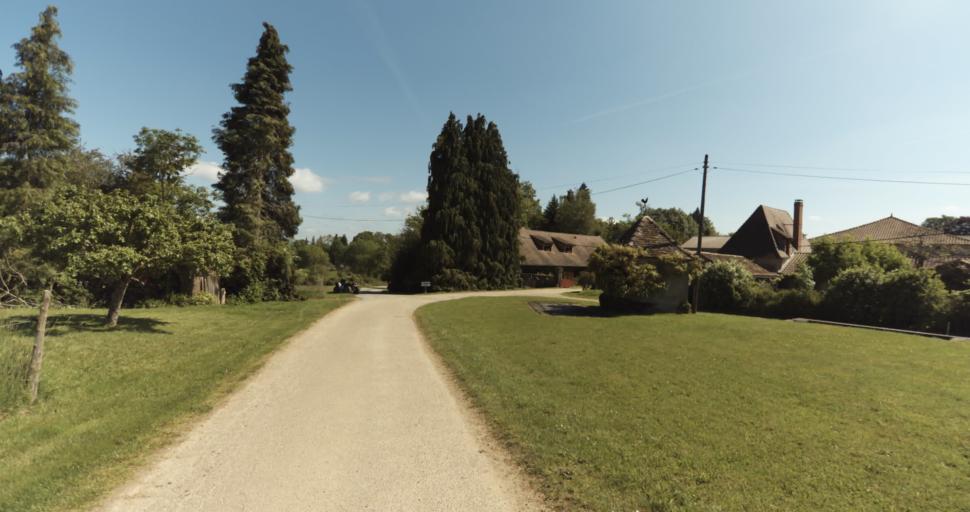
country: FR
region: Limousin
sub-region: Departement de la Haute-Vienne
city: Le Vigen
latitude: 45.7227
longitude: 1.2986
